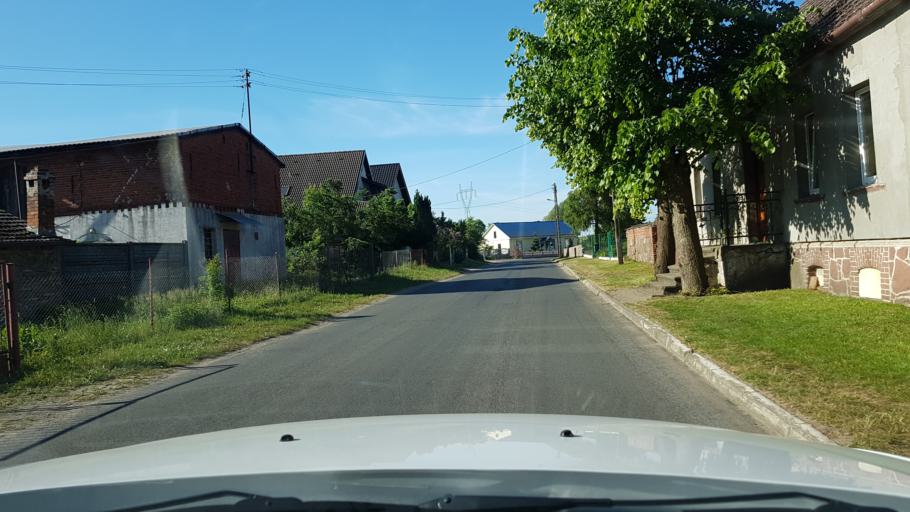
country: PL
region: West Pomeranian Voivodeship
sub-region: Powiat pyrzycki
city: Bielice
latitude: 53.2185
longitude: 14.6100
